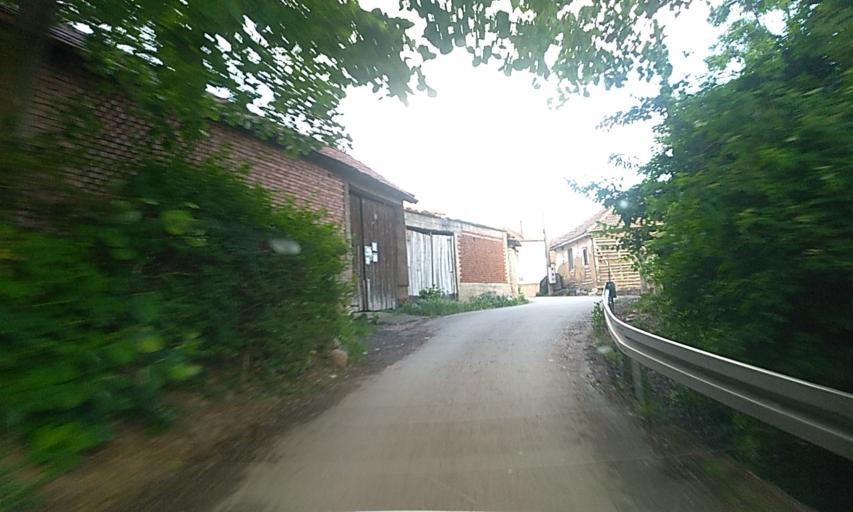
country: RS
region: Central Serbia
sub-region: Nisavski Okrug
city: Nis
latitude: 43.3691
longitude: 21.9674
